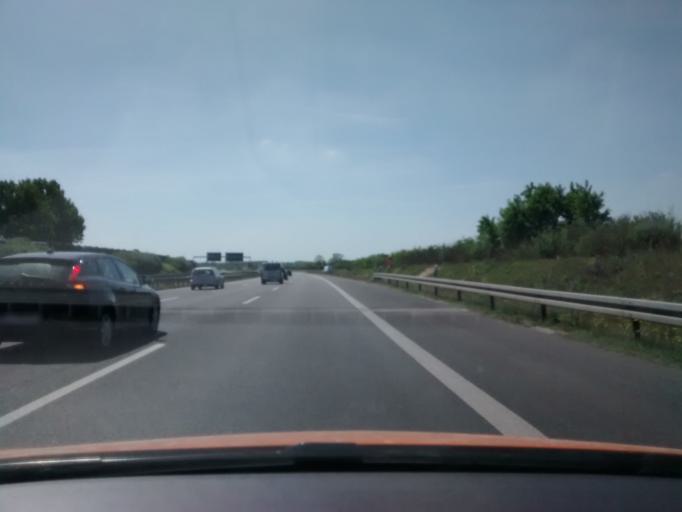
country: DE
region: Brandenburg
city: Schulzendorf
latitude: 52.3641
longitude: 13.5481
